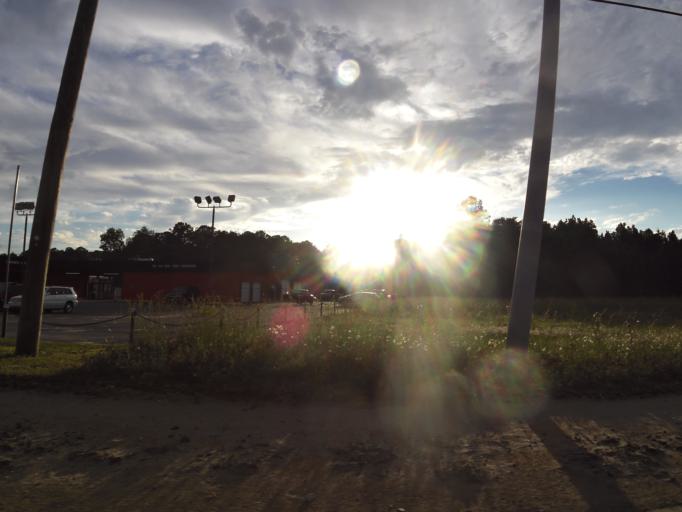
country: US
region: Georgia
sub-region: Chatham County
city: Garden City
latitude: 32.0796
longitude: -81.1958
